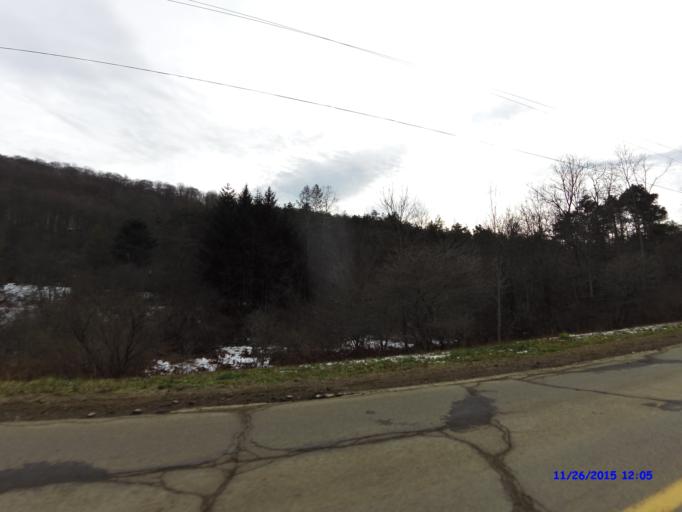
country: US
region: New York
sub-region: Cattaraugus County
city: Franklinville
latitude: 42.2249
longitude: -78.4473
